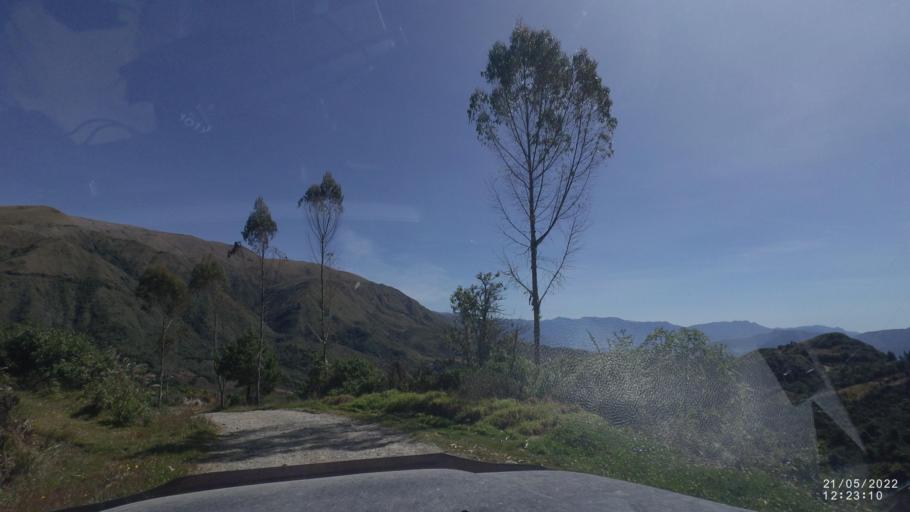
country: BO
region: Cochabamba
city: Colomi
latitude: -17.2215
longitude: -65.9044
